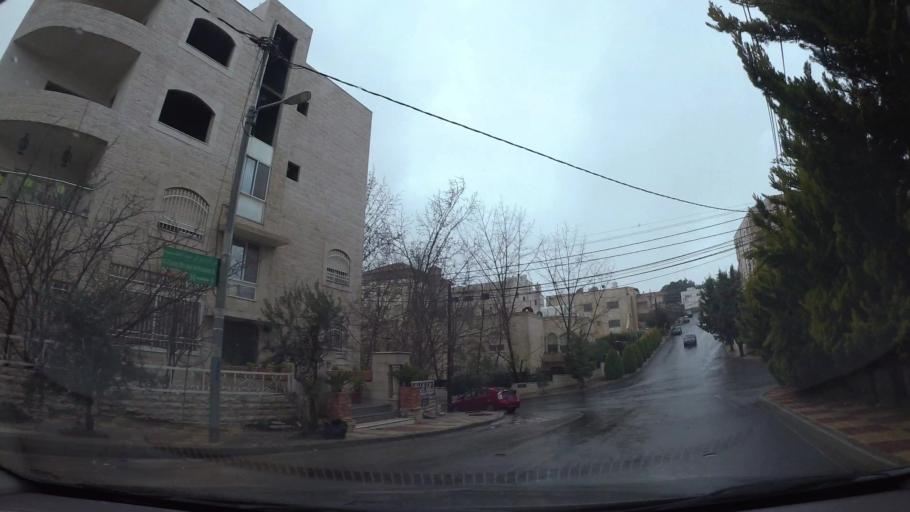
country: JO
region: Amman
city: Al Jubayhah
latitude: 32.0240
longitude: 35.8817
